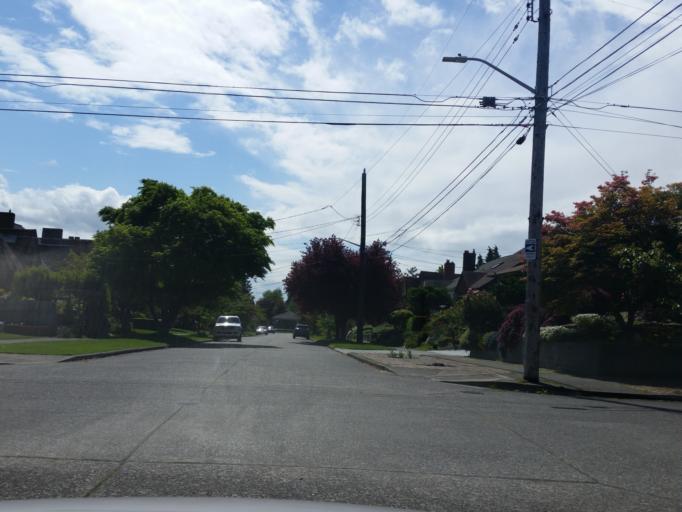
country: US
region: Washington
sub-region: King County
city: Shoreline
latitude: 47.6851
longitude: -122.3994
